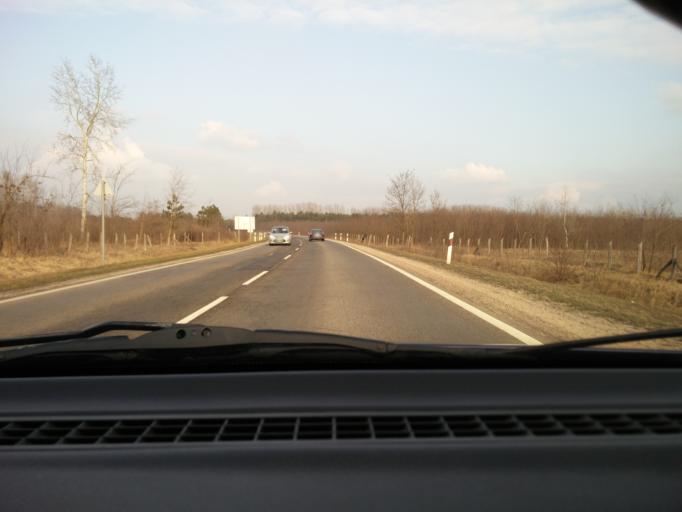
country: HU
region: Pest
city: Ujhartyan
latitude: 47.2287
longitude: 19.4170
